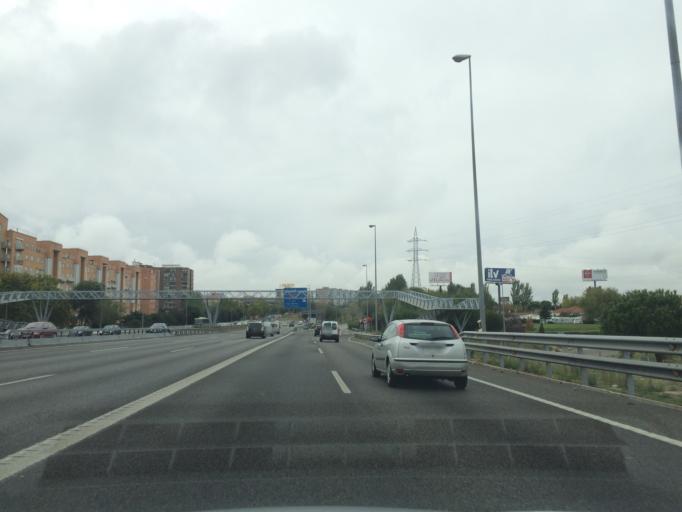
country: ES
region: Madrid
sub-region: Provincia de Madrid
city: Alcorcon
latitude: 40.3567
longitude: -3.8203
